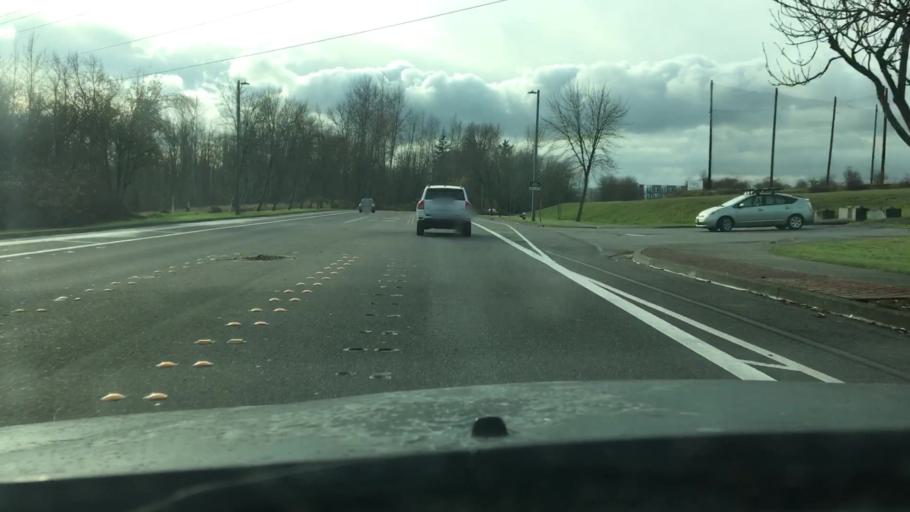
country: US
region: Washington
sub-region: Whatcom County
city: Geneva
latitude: 48.7741
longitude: -122.4368
